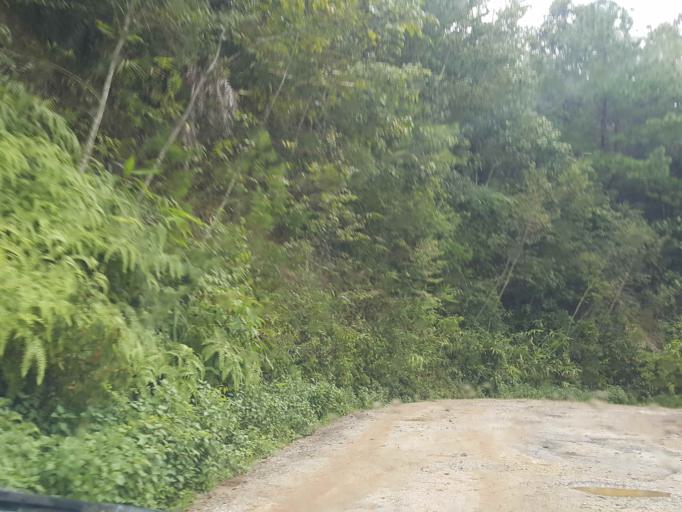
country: TH
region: Chiang Mai
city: Mae Chaem
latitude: 18.5076
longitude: 98.5267
